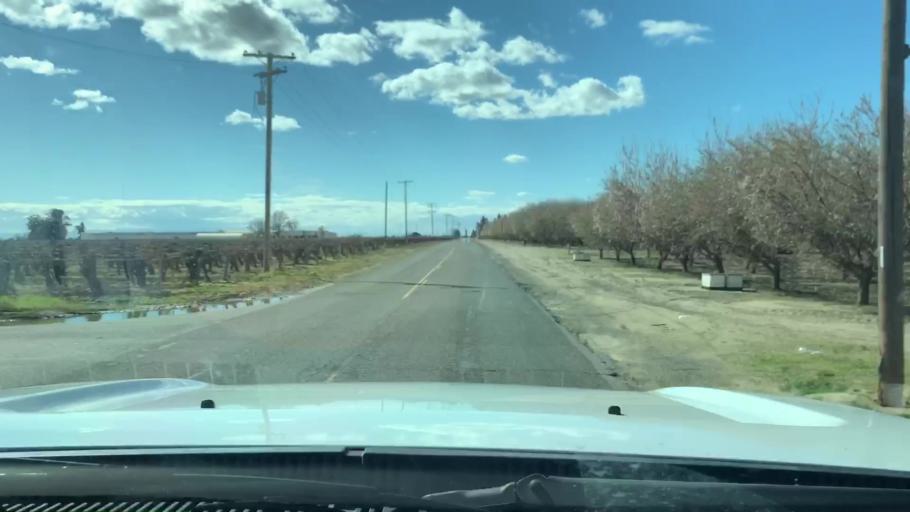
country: US
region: California
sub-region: Fresno County
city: Fowler
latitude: 36.5619
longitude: -119.7290
